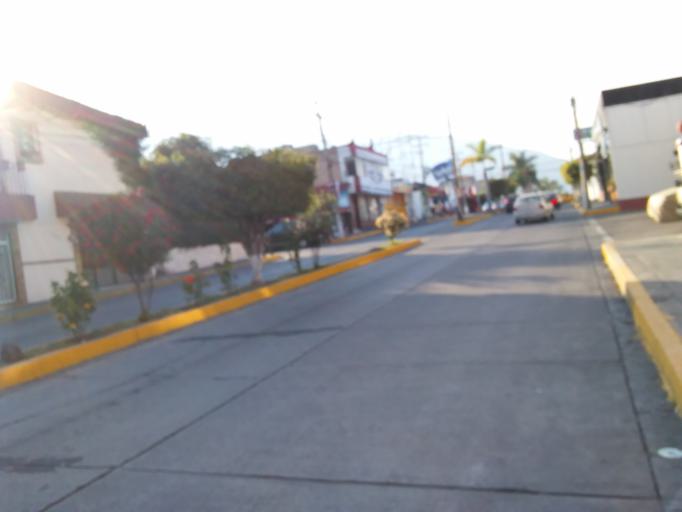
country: MX
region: Nayarit
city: Tepic
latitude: 21.5006
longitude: -104.9020
